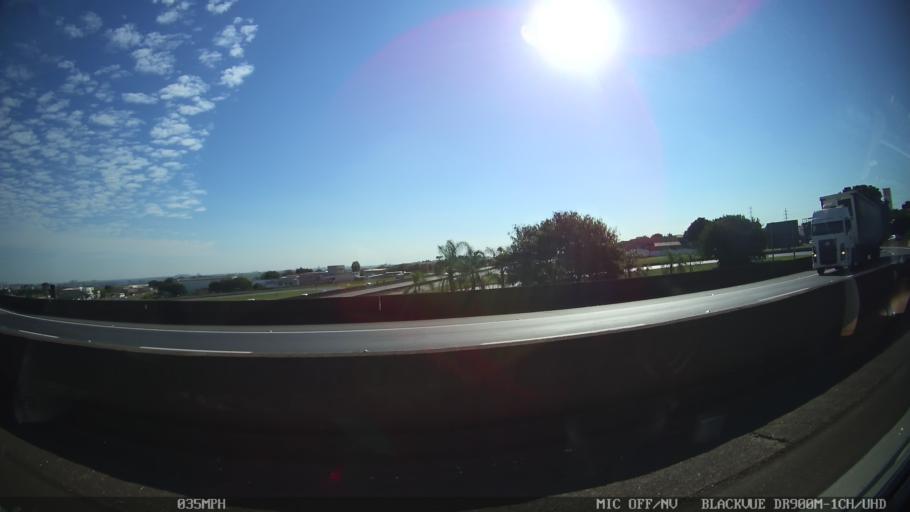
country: BR
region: Sao Paulo
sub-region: Nova Odessa
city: Nova Odessa
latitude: -22.7536
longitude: -47.2573
